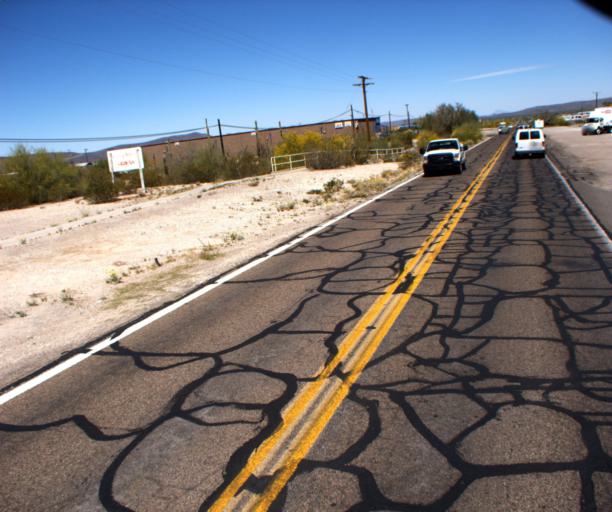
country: US
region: Arizona
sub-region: Pima County
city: Ajo
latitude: 32.3907
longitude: -112.8722
